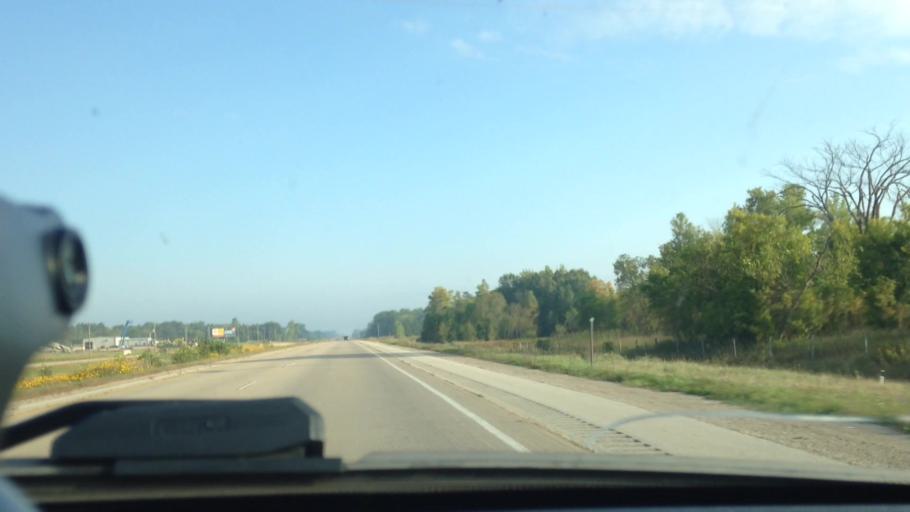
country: US
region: Wisconsin
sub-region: Oconto County
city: Oconto Falls
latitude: 44.9942
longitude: -88.0451
